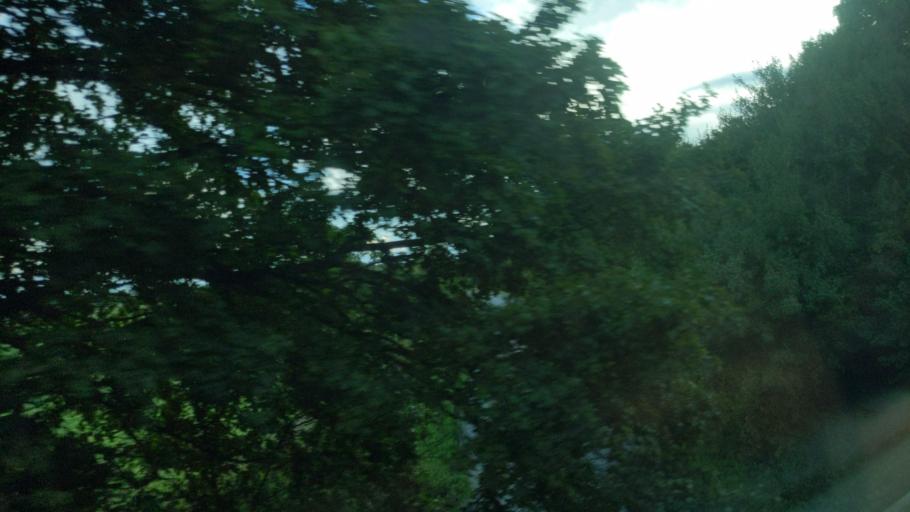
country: CZ
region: Central Bohemia
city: Uvaly
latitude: 50.0767
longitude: 14.7618
